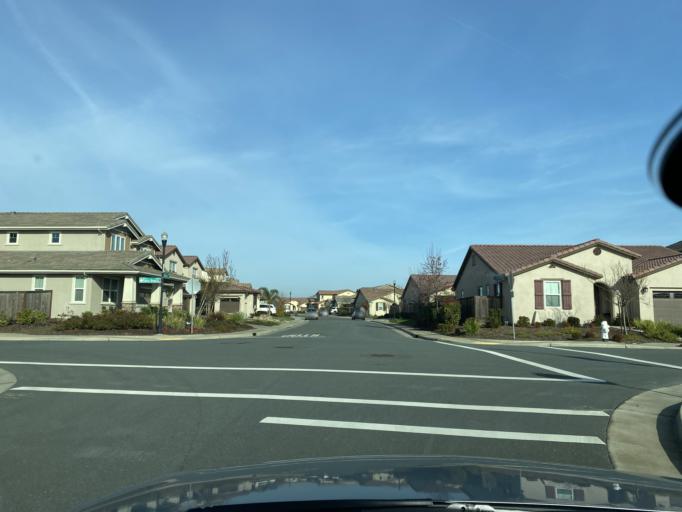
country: US
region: California
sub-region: Sacramento County
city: Elk Grove
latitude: 38.3975
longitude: -121.3859
